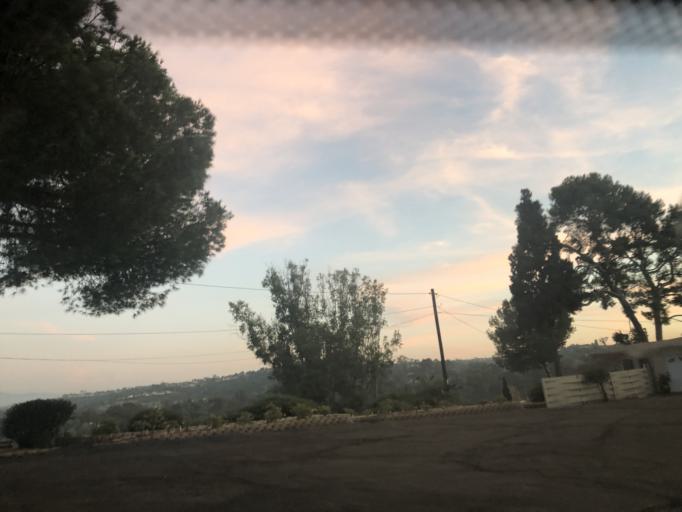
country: US
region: California
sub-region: San Diego County
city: Bonita
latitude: 32.6620
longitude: -117.0433
